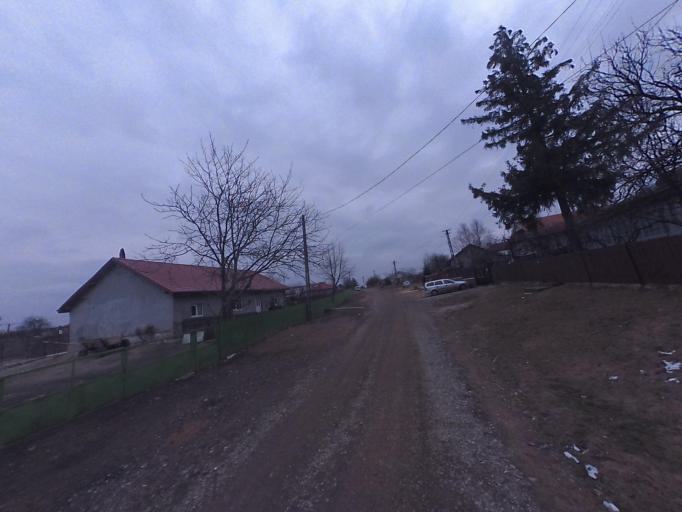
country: RO
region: Iasi
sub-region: Comuna Popricani
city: Popricani
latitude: 47.2933
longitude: 27.5018
